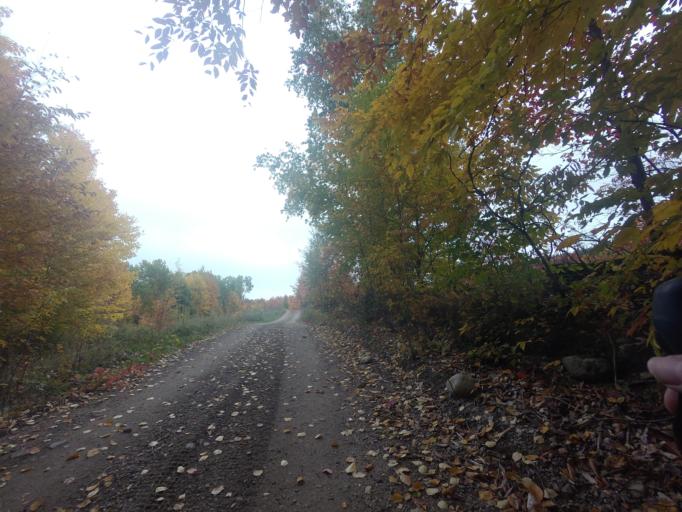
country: CA
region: Ontario
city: Pembroke
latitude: 45.7302
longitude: -77.2279
